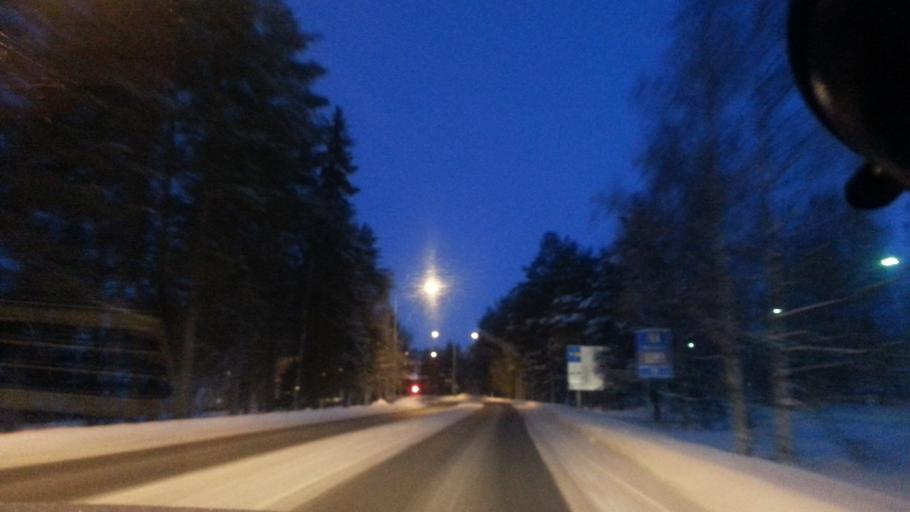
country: FI
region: Lapland
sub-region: Rovaniemi
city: Rovaniemi
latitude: 66.4952
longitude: 25.7566
